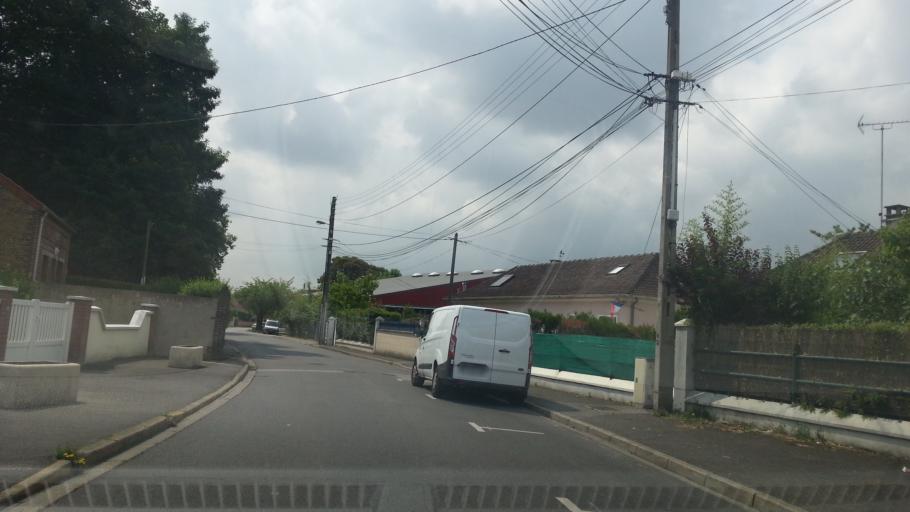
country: FR
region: Picardie
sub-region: Departement de l'Oise
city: Montataire
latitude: 49.2581
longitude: 2.4517
